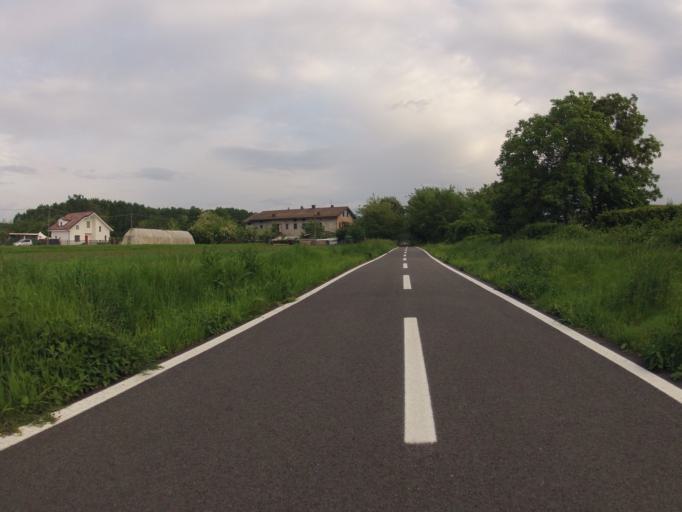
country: IT
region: Piedmont
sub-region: Provincia di Torino
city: Villafranca Piemonte
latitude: 44.7884
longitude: 7.5093
